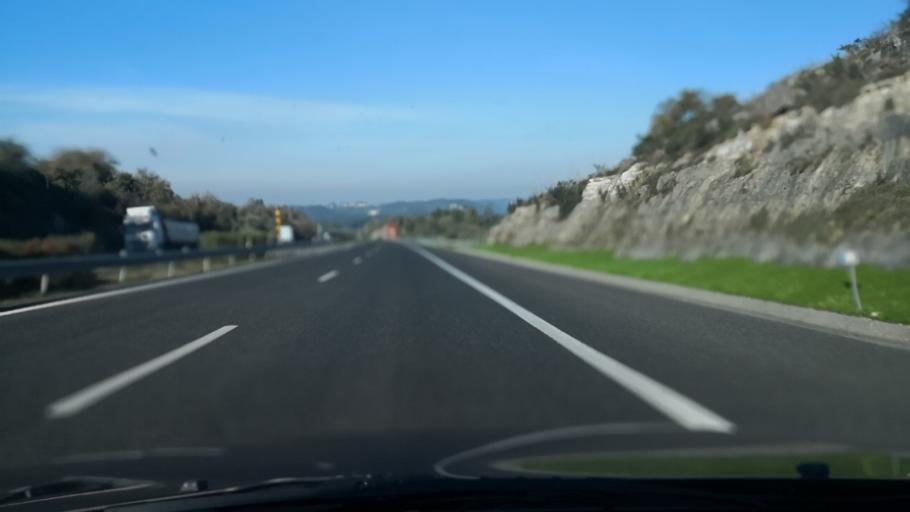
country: PT
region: Leiria
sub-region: Leiria
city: Santa Catarina da Serra
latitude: 39.6900
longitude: -8.6900
